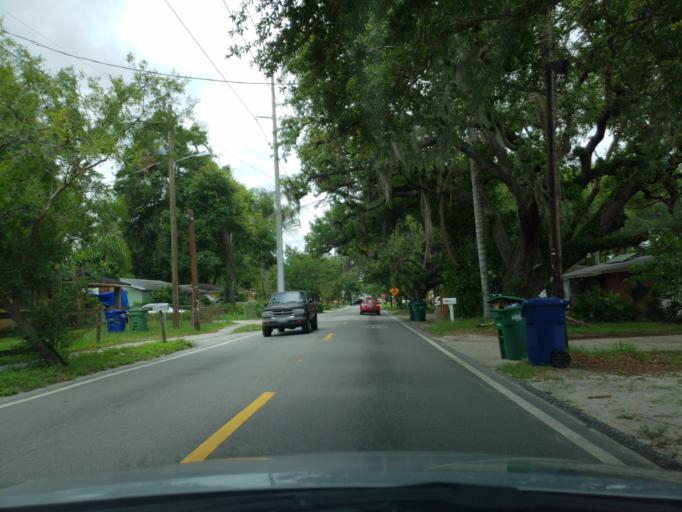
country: US
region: Florida
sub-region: Hillsborough County
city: Tampa
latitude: 28.0034
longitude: -82.4414
